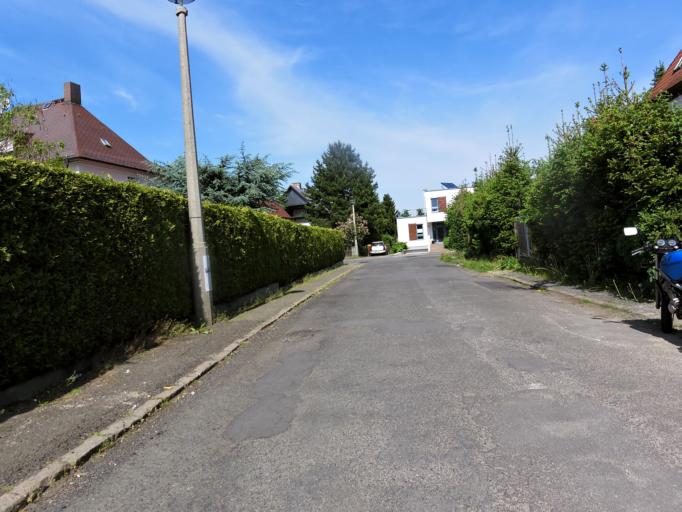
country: DE
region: Saxony
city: Leipzig
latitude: 51.3115
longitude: 12.4288
